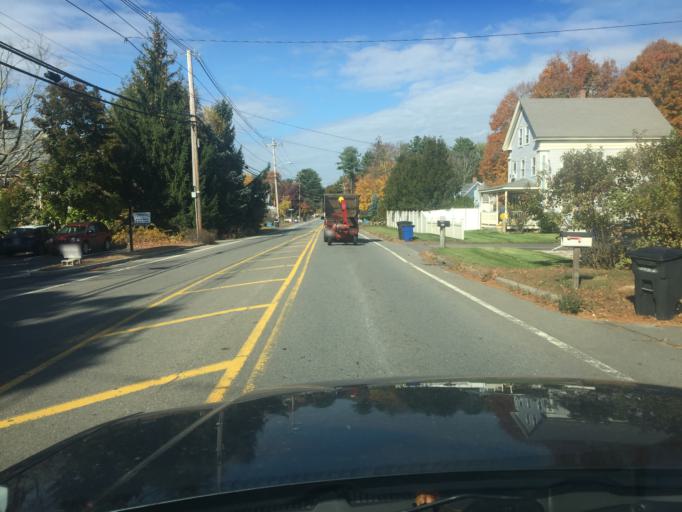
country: US
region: Massachusetts
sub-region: Norfolk County
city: Bellingham
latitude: 42.1039
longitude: -71.5044
